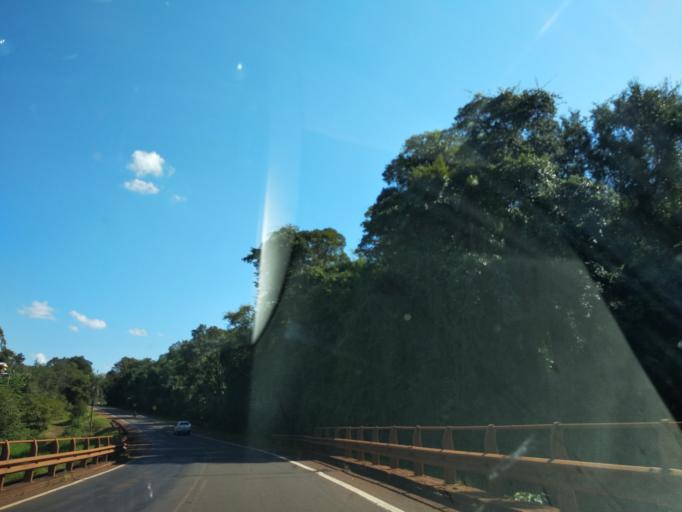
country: AR
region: Misiones
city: Puerto Piray
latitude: -26.4809
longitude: -54.6572
